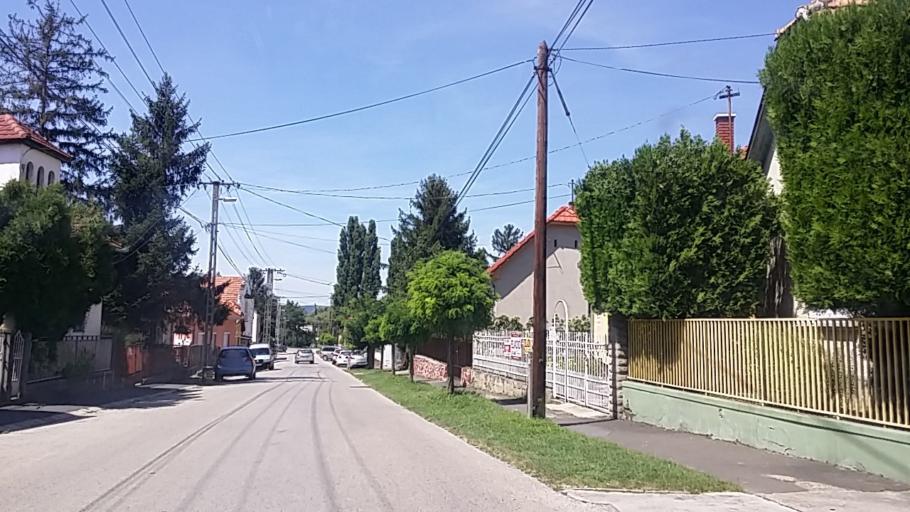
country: HU
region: Somogy
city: Balatonlelle
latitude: 46.7841
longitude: 17.6963
